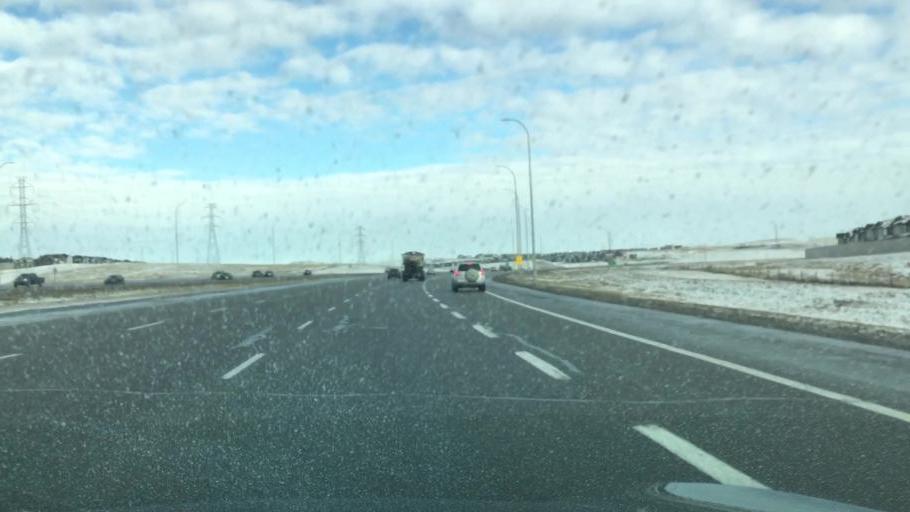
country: CA
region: Alberta
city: Calgary
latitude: 51.1699
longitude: -114.1019
